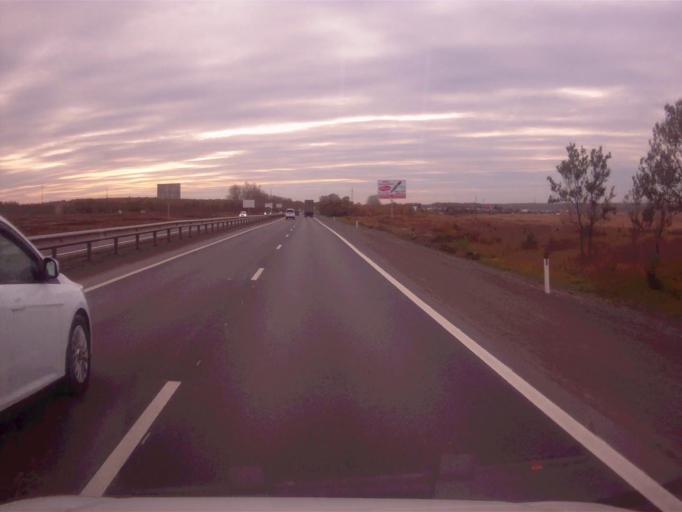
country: RU
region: Chelyabinsk
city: Roza
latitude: 54.9882
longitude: 61.4391
